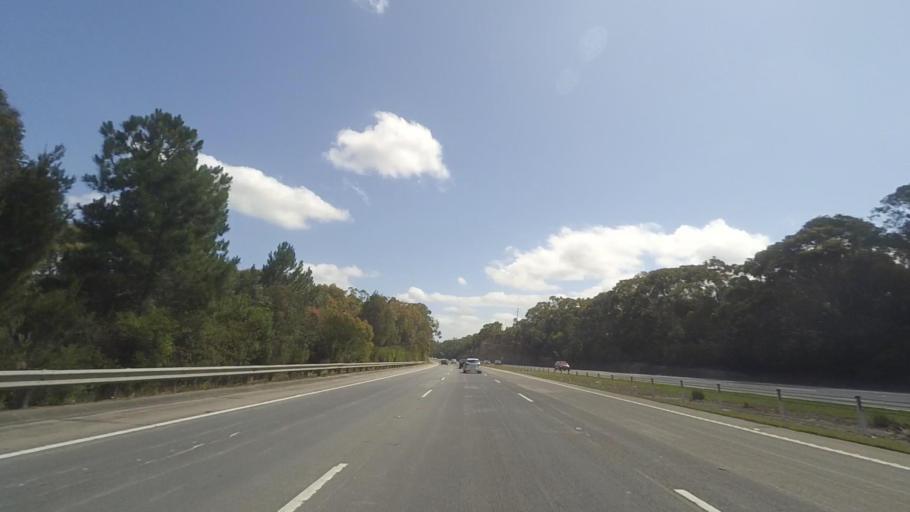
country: AU
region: New South Wales
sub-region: Hornsby Shire
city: Mount Colah
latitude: -33.6639
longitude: 151.1250
